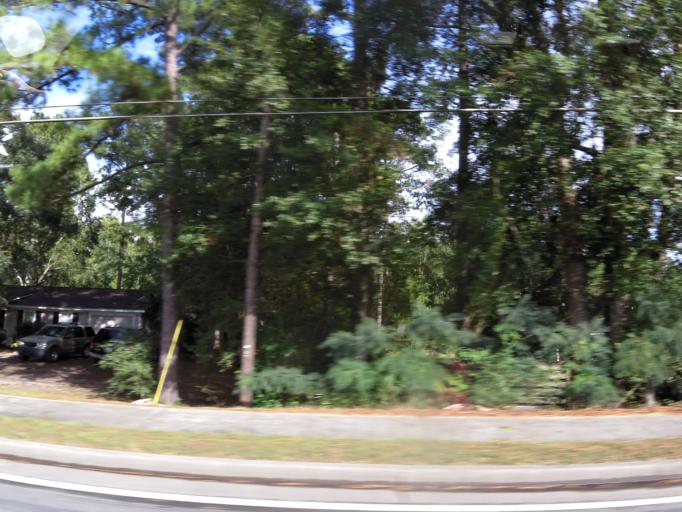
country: US
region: Georgia
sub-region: Liberty County
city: Hinesville
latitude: 31.8374
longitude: -81.5954
